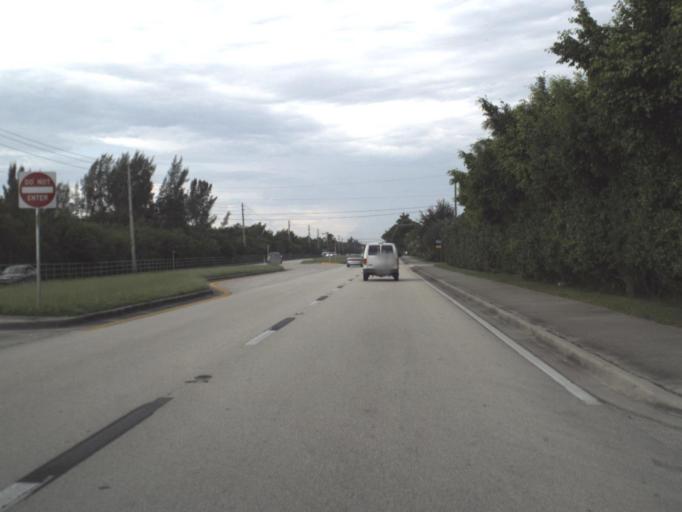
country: US
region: Florida
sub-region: Lee County
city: Harlem Heights
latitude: 26.5363
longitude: -81.9223
